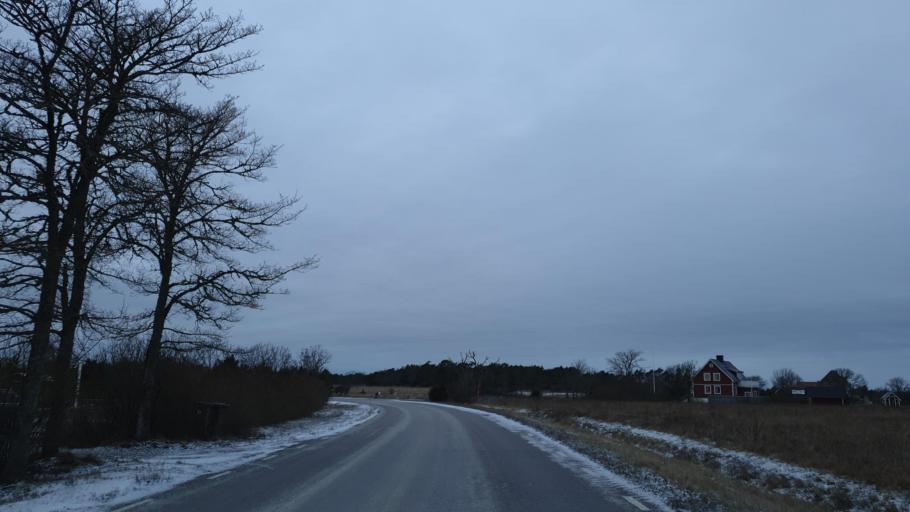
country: SE
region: Gotland
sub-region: Gotland
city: Slite
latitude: 57.4226
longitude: 18.9044
